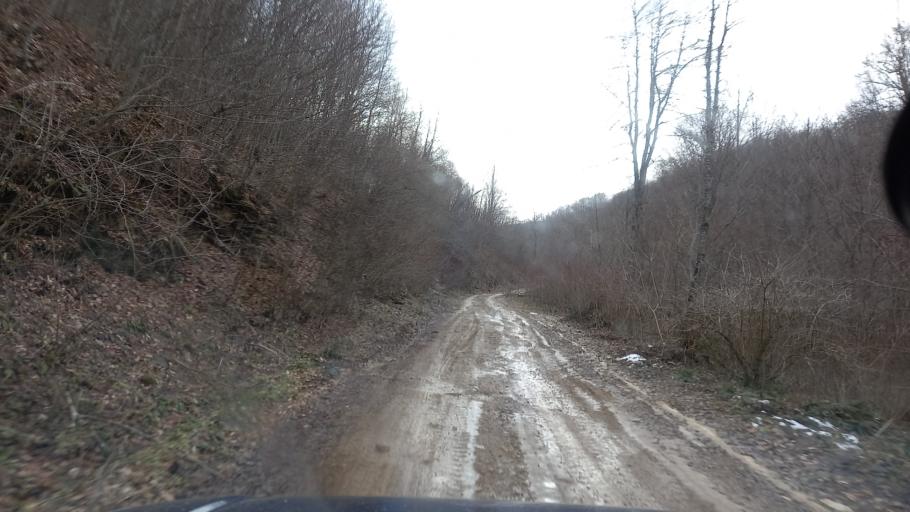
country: RU
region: Adygeya
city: Kamennomostskiy
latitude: 44.1728
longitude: 40.2996
